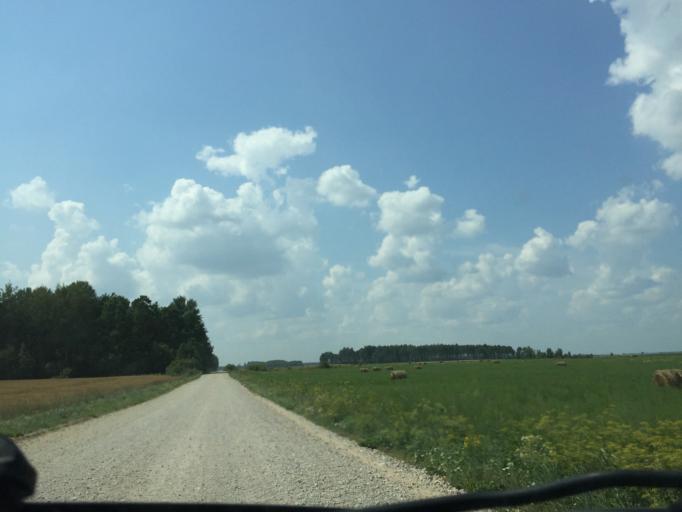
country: LT
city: Zagare
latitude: 56.3946
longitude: 23.2073
